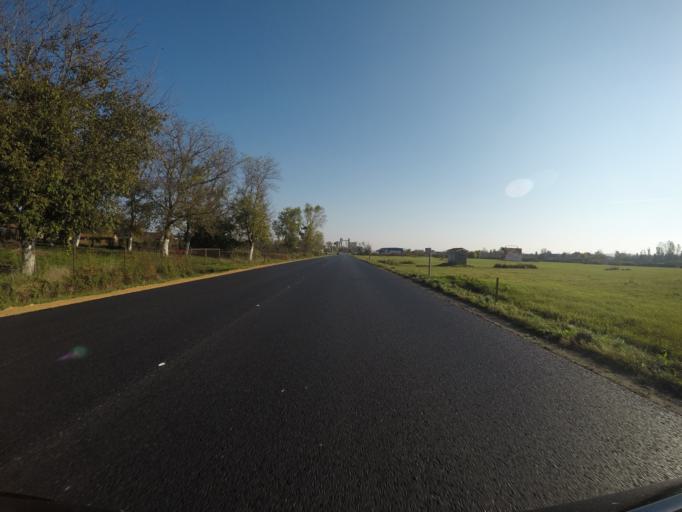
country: HR
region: Koprivnicko-Krizevacka
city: Kalinovac
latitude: 46.0355
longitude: 17.0588
